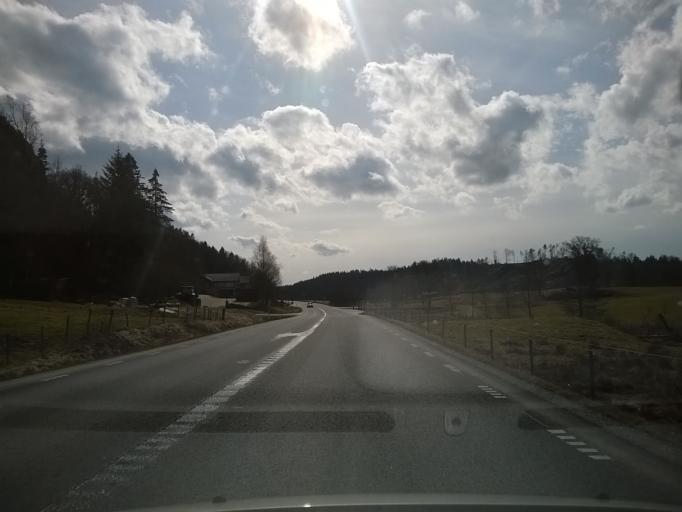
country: SE
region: Vaestra Goetaland
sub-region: Orust
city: Henan
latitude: 58.2036
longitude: 11.6898
